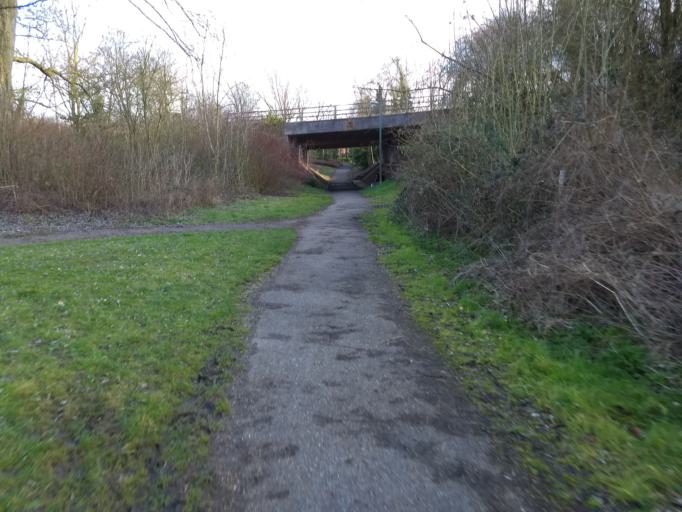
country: GB
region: England
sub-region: Milton Keynes
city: Milton Keynes
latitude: 52.0470
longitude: -0.7308
